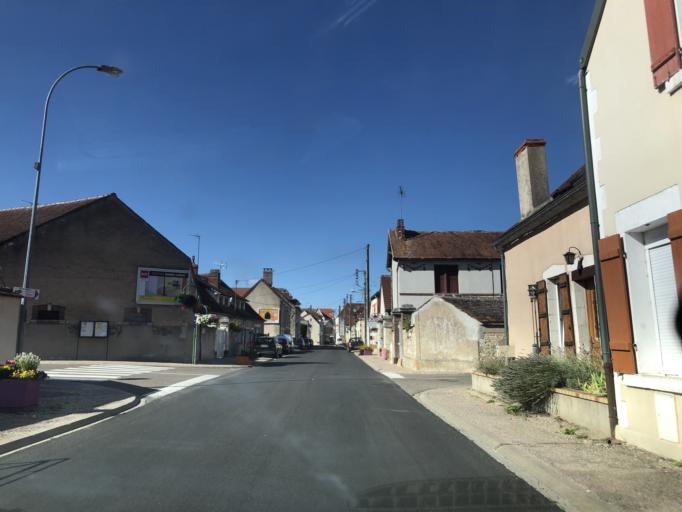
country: FR
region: Bourgogne
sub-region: Departement de l'Yonne
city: Appoigny
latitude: 47.8741
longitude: 3.5267
